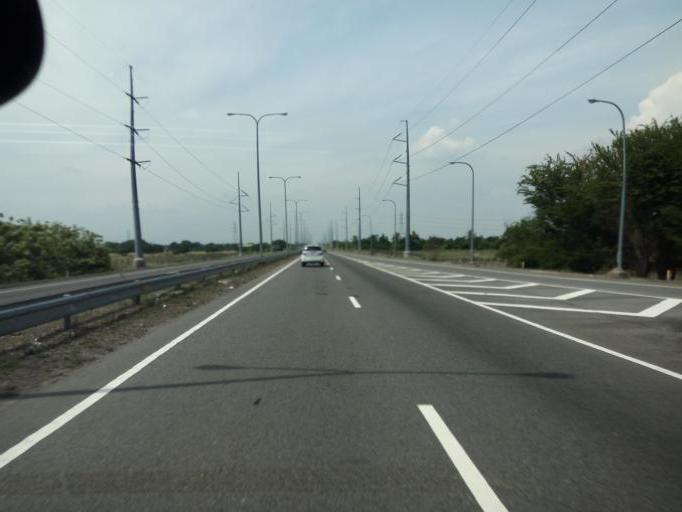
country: PH
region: Central Luzon
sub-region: Province of Tarlac
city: Santo Nino
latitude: 15.3190
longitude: 120.6251
